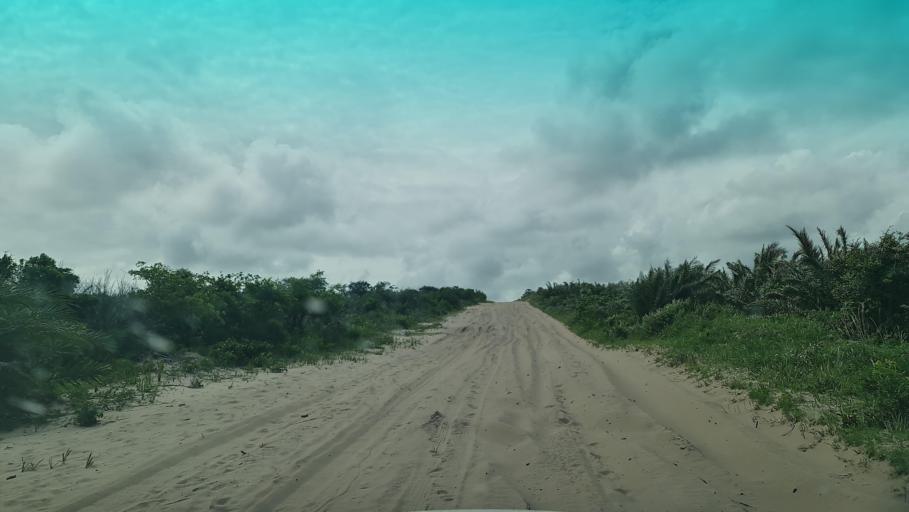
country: MZ
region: Maputo
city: Manhica
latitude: -25.4480
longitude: 32.9518
